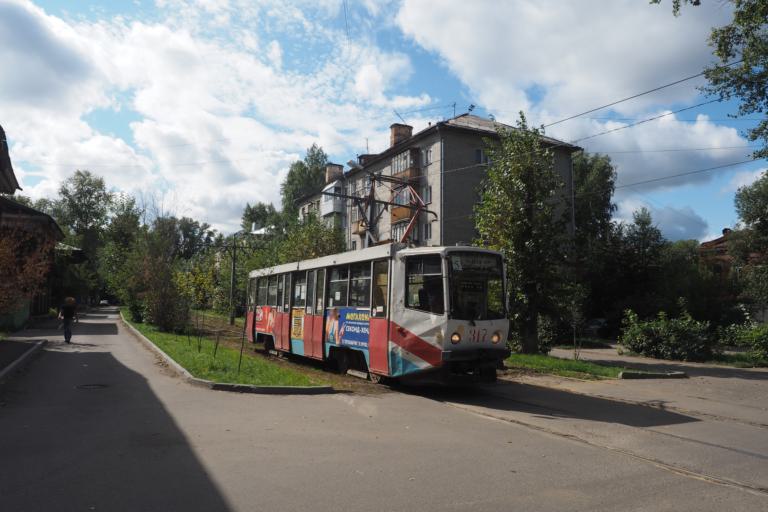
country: RU
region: Tomsk
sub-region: Tomskiy Rayon
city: Tomsk
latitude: 56.4830
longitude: 84.9534
